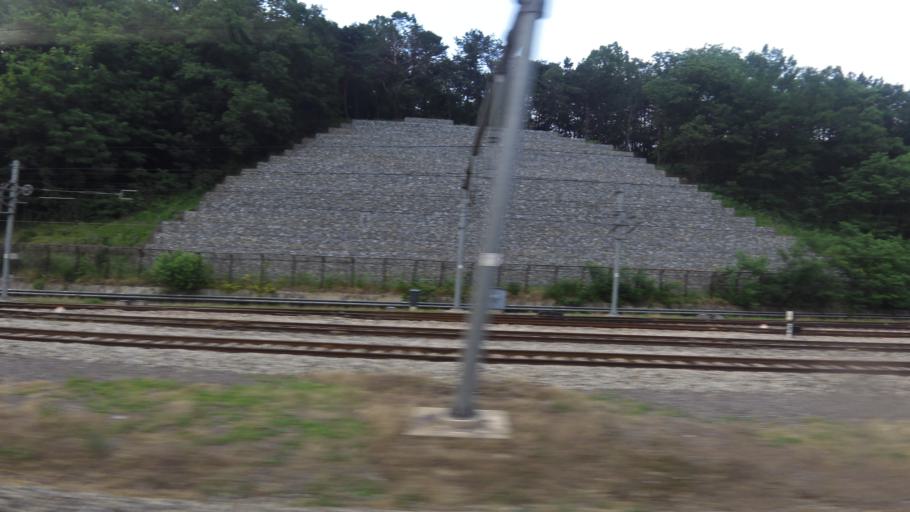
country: KR
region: Daejeon
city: Sintansin
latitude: 36.5000
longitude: 127.3896
